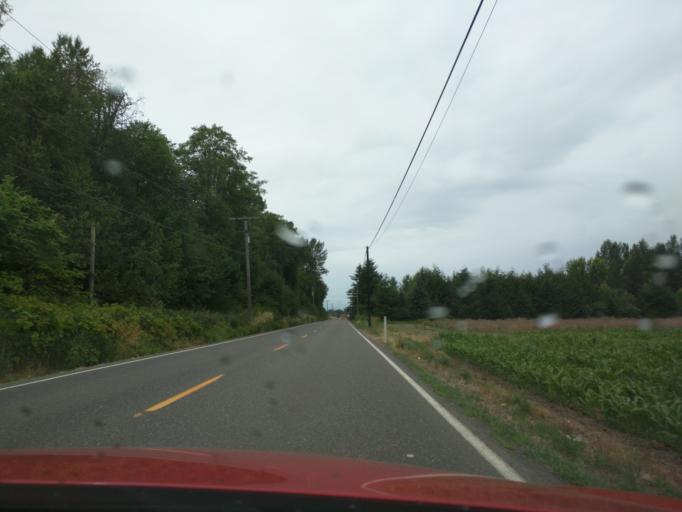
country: US
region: Washington
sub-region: Whatcom County
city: Nooksack
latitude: 48.8953
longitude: -122.3205
